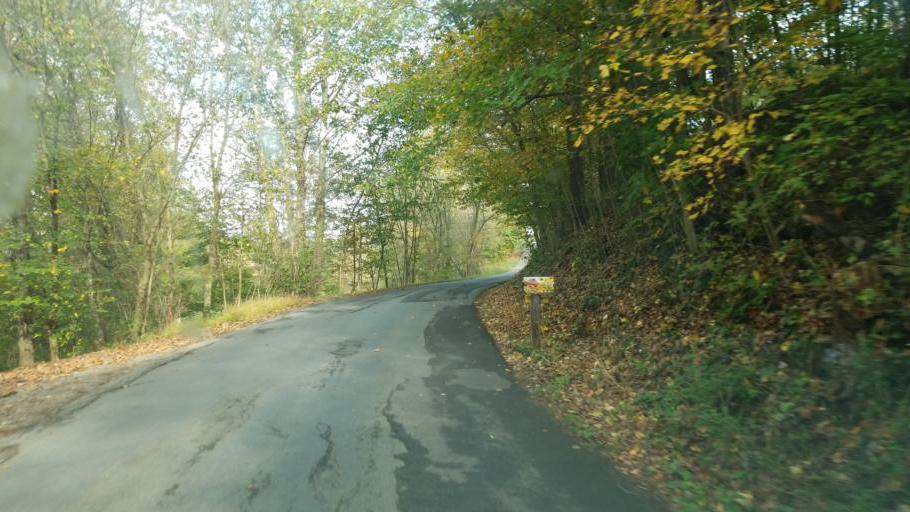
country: US
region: Ohio
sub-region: Holmes County
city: Millersburg
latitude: 40.5417
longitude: -81.8810
